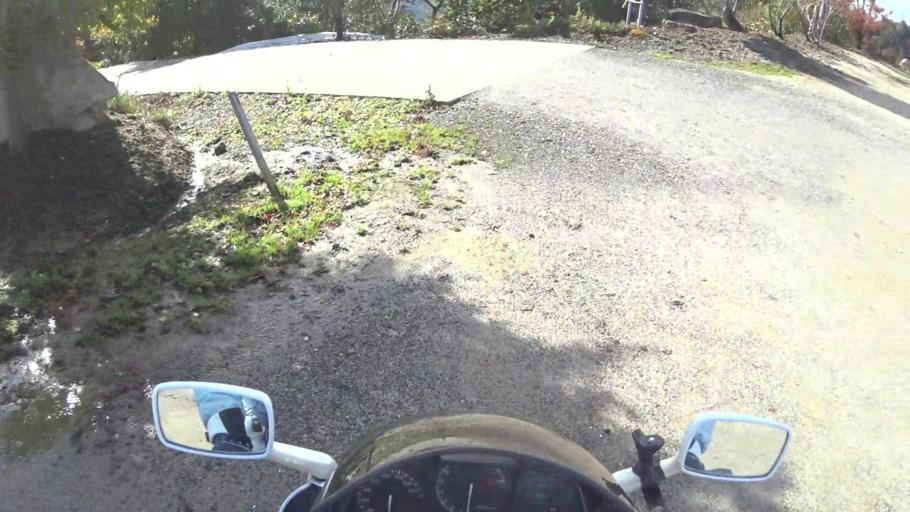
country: JP
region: Kyoto
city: Miyazu
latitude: 35.6015
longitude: 135.1883
